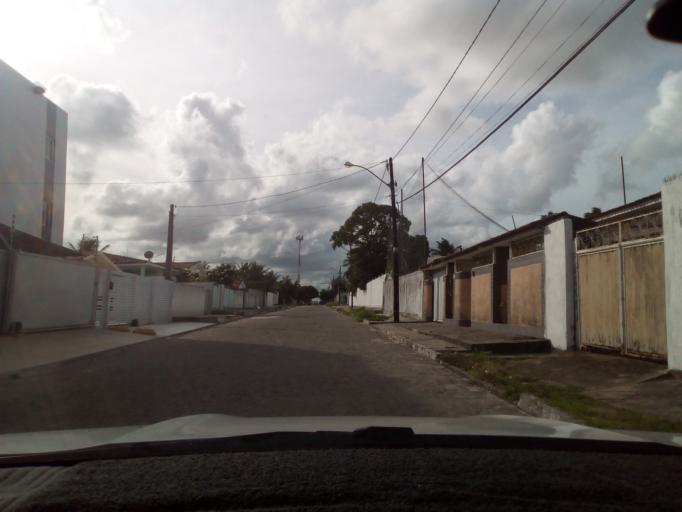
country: BR
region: Paraiba
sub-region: Joao Pessoa
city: Joao Pessoa
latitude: -7.1548
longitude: -34.8778
